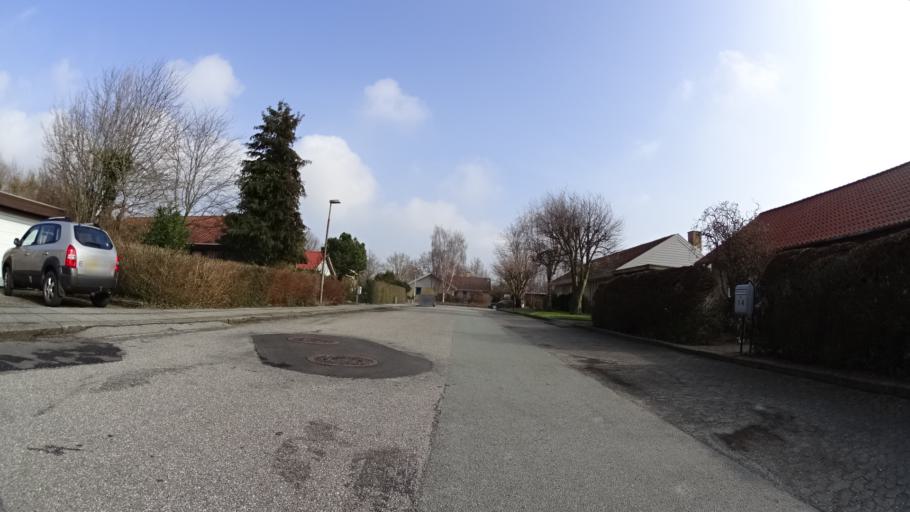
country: DK
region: Central Jutland
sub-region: Arhus Kommune
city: Tranbjerg
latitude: 56.0886
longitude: 10.1396
